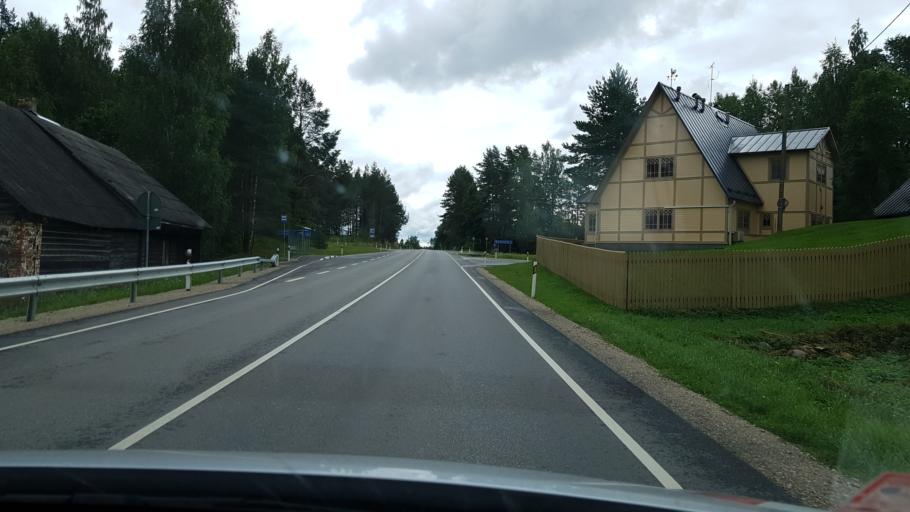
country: EE
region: Polvamaa
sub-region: Polva linn
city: Polva
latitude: 58.0135
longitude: 27.1731
